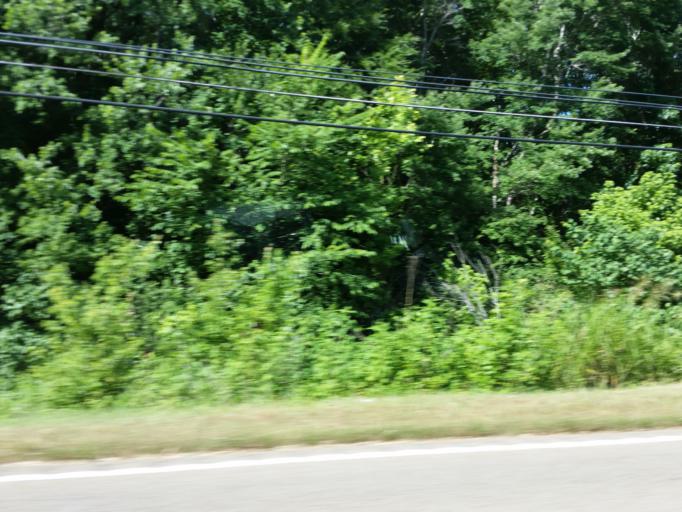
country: US
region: Tennessee
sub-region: Decatur County
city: Parsons
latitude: 35.6451
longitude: -88.1010
